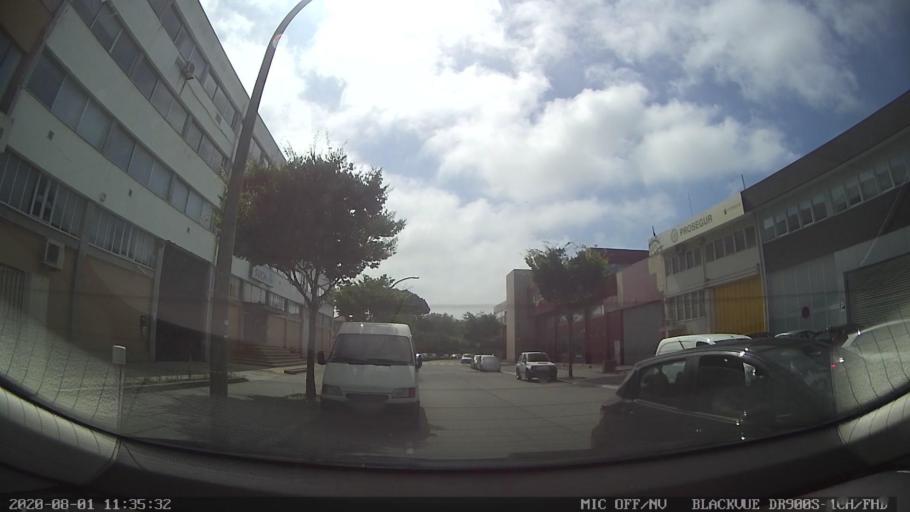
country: PT
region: Porto
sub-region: Matosinhos
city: Senhora da Hora
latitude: 41.1728
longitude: -8.6433
